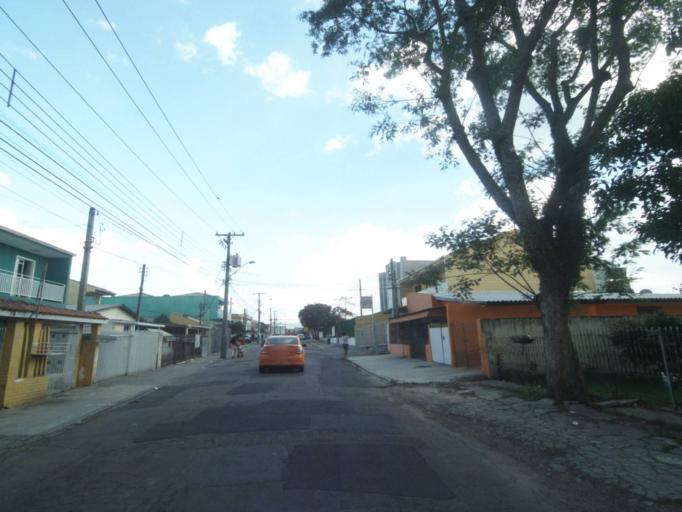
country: BR
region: Parana
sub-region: Sao Jose Dos Pinhais
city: Sao Jose dos Pinhais
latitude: -25.5330
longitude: -49.2704
